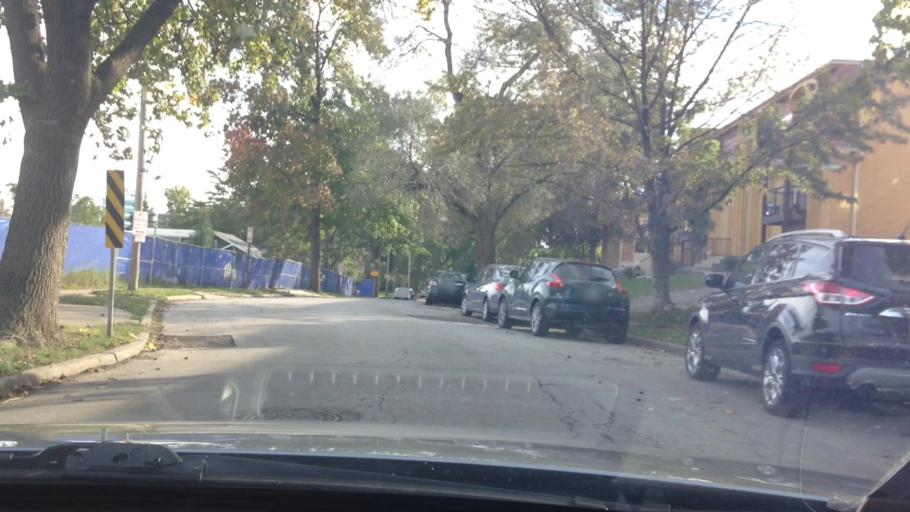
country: US
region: Kansas
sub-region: Johnson County
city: Westwood
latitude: 39.0476
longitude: -94.5933
